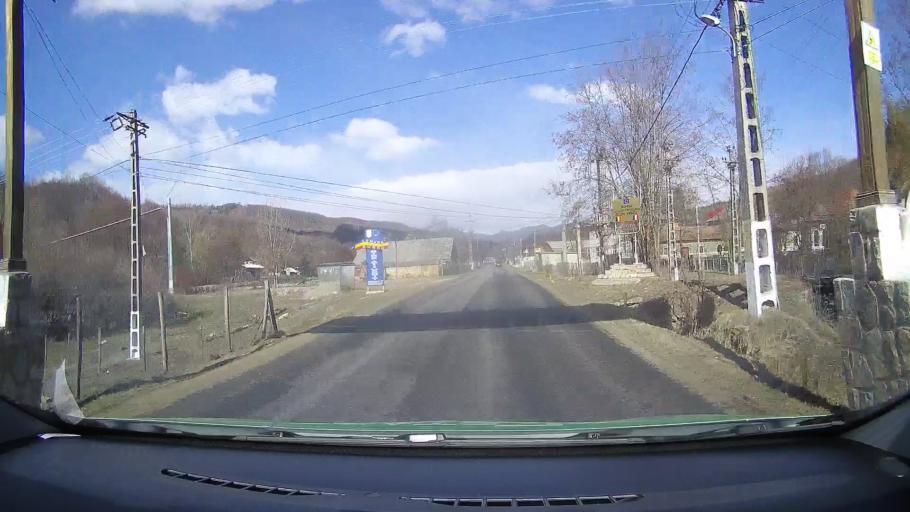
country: RO
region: Dambovita
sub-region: Comuna Runcu
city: Badeni
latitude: 45.1503
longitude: 25.4021
